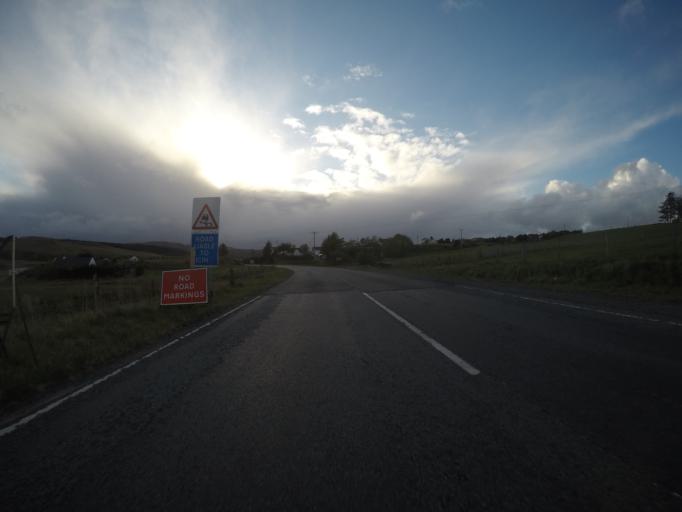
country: GB
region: Scotland
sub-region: Highland
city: Isle of Skye
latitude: 57.4532
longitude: -6.2945
